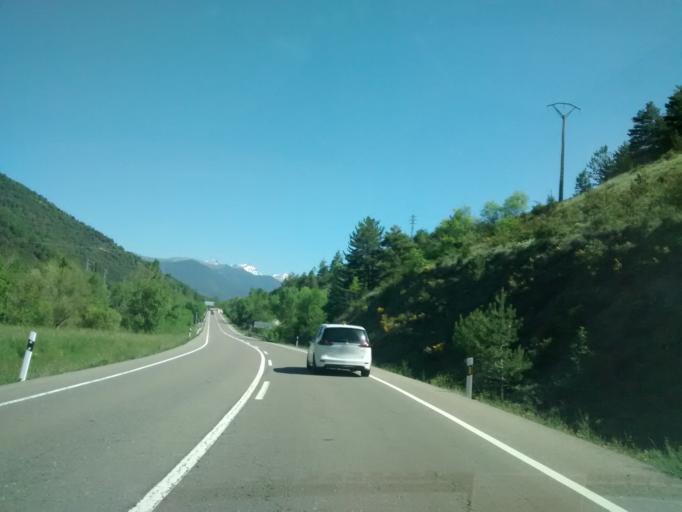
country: ES
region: Aragon
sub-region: Provincia de Huesca
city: Jaca
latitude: 42.5921
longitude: -0.5431
